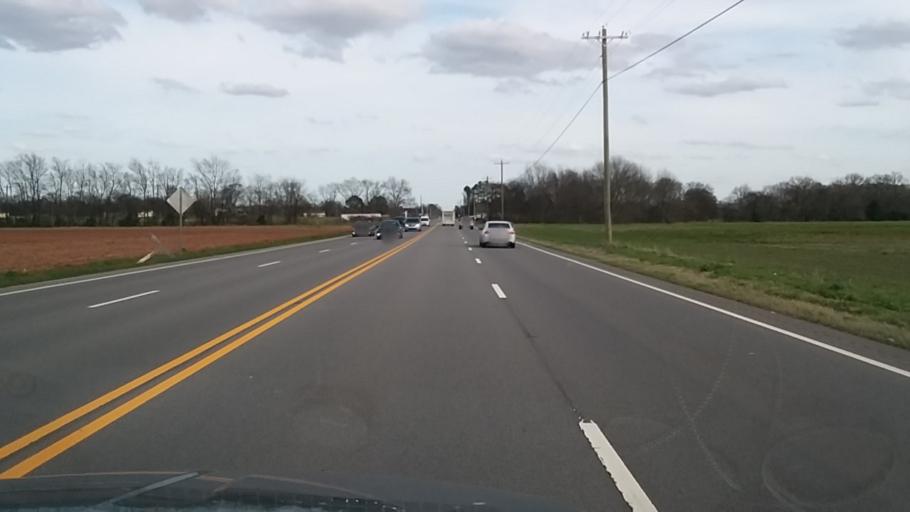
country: US
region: Alabama
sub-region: Lawrence County
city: Town Creek
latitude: 34.6816
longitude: -87.4253
